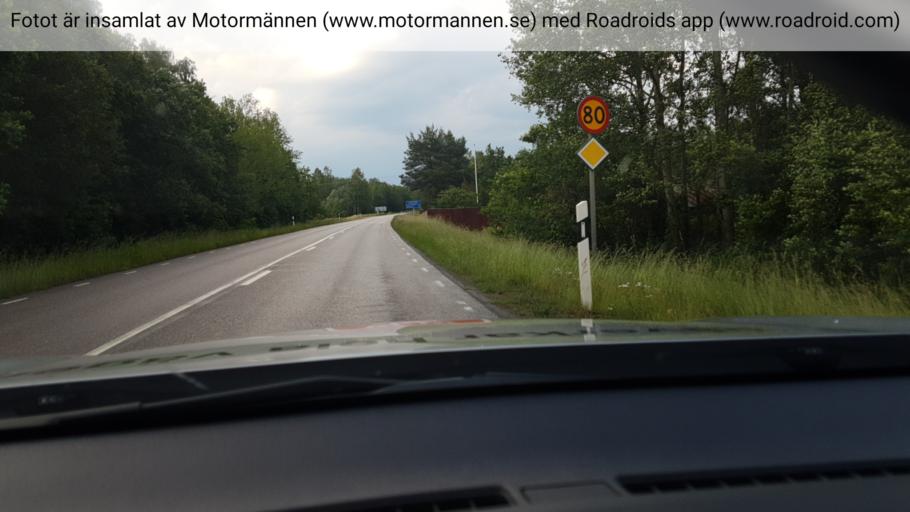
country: SE
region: Vaestra Goetaland
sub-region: Hjo Kommun
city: Hjo
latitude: 58.3051
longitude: 14.2555
